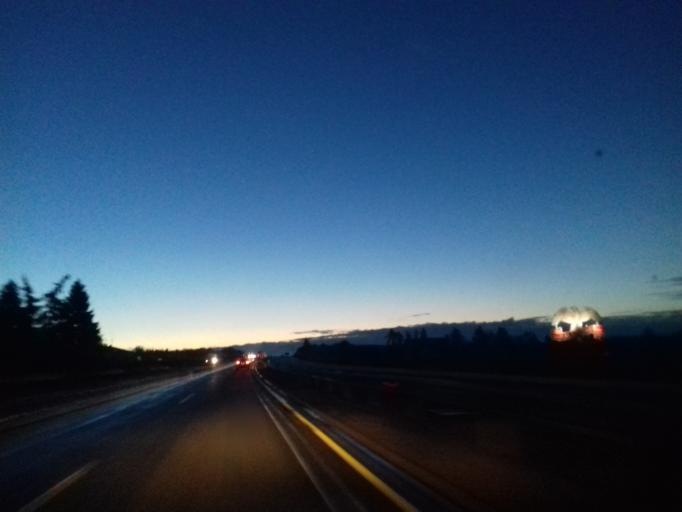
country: CZ
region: Vysocina
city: Merin
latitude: 49.3884
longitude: 15.9159
